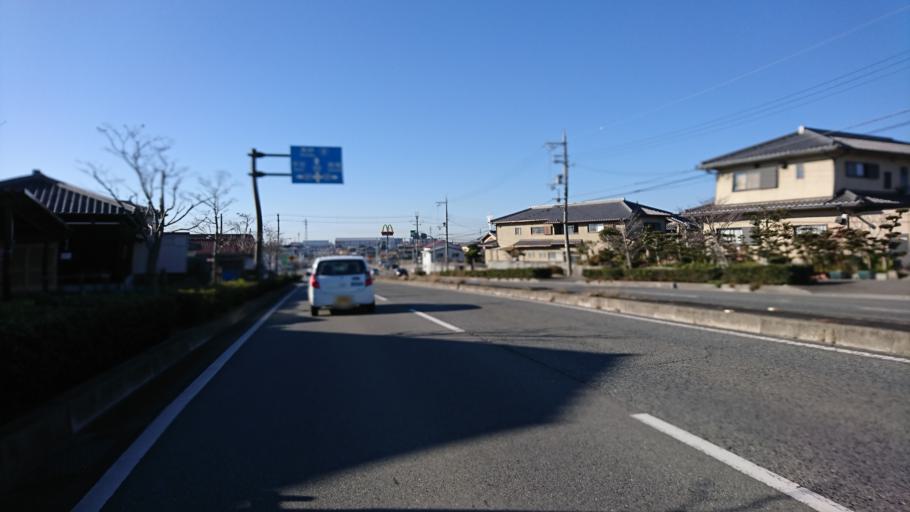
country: JP
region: Hyogo
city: Kakogawacho-honmachi
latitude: 34.7956
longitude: 134.8263
